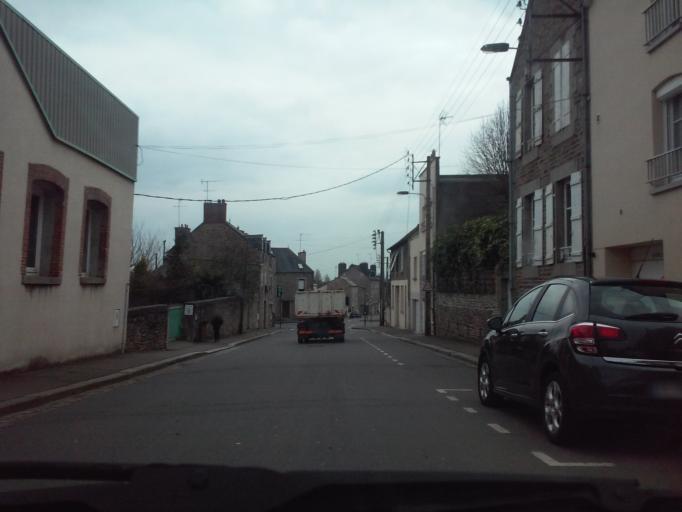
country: FR
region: Brittany
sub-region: Departement d'Ille-et-Vilaine
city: Fougeres
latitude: 48.3482
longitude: -1.1891
